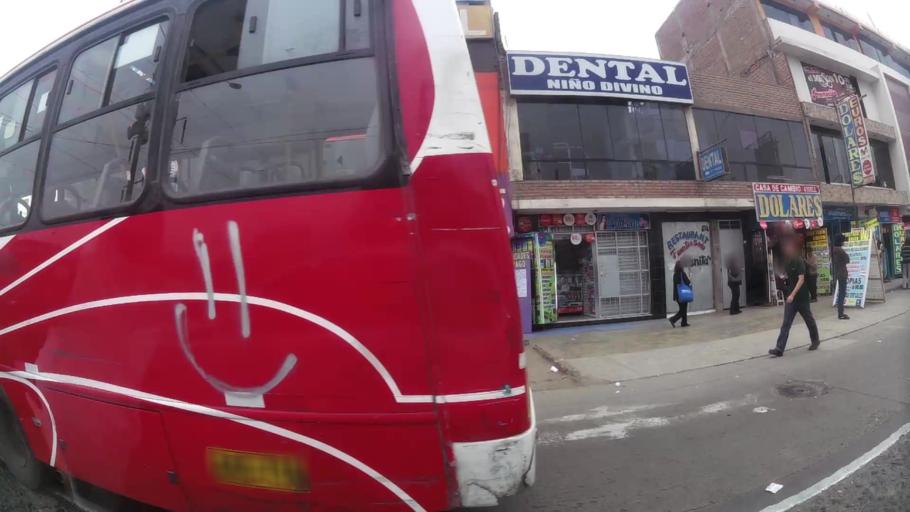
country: PE
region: Lima
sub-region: Lima
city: Independencia
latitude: -11.9763
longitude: -77.0832
